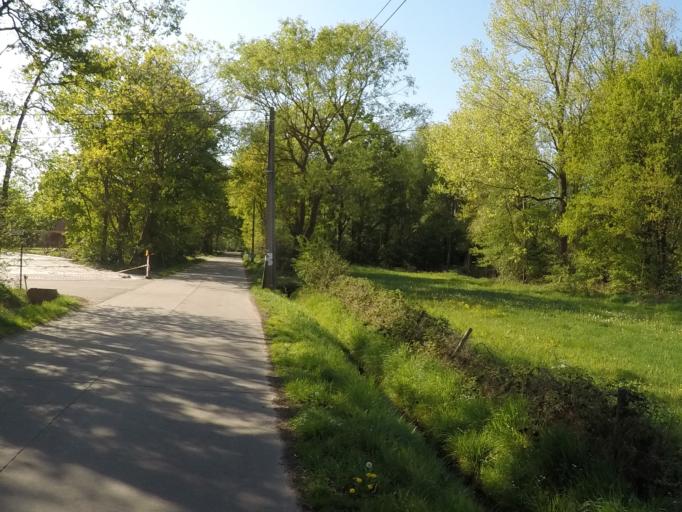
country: BE
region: Flanders
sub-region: Provincie Antwerpen
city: Nijlen
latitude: 51.1513
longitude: 4.6578
